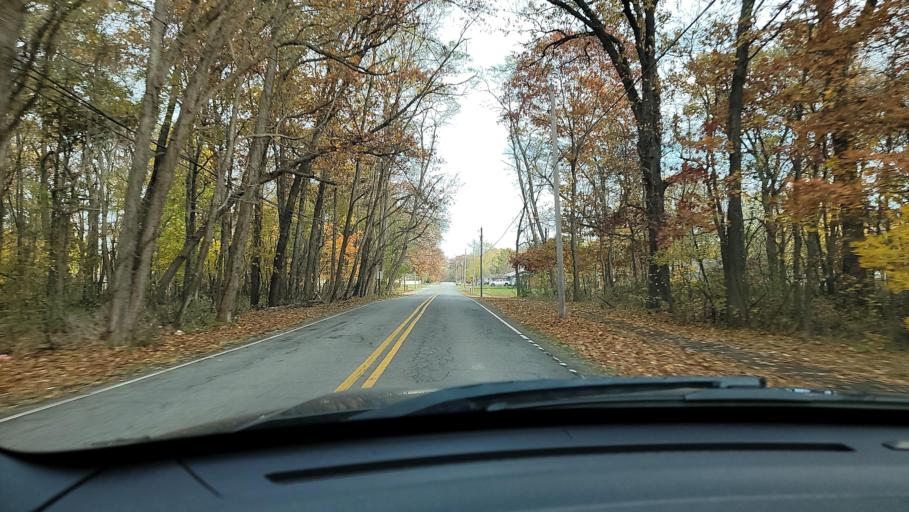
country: US
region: Indiana
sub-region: Porter County
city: Portage
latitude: 41.5942
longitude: -87.1623
